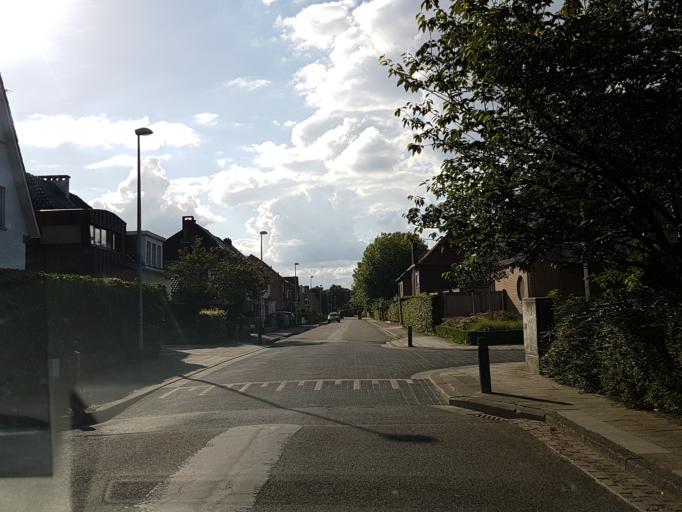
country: BE
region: Flanders
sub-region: Provincie Antwerpen
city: Mechelen
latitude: 51.0440
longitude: 4.4840
